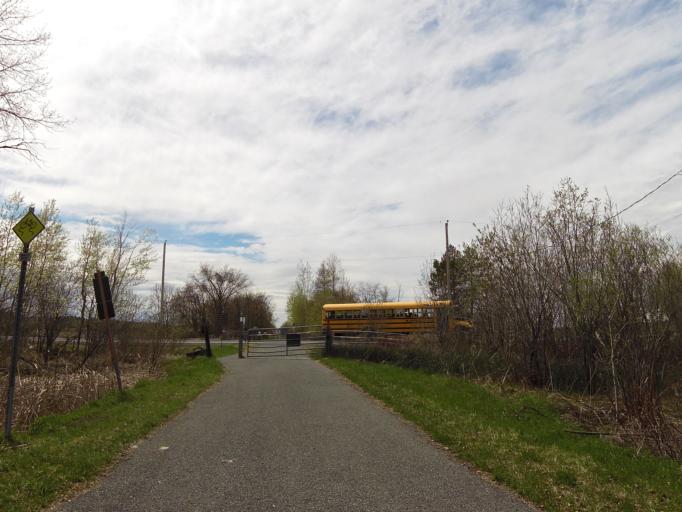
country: CA
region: Ontario
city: Hawkesbury
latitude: 45.5330
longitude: -74.6603
